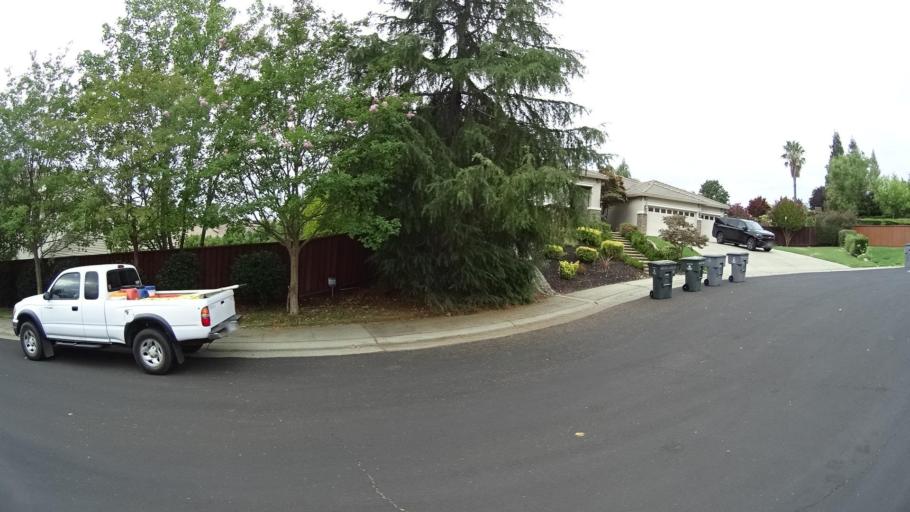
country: US
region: California
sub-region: Placer County
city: Rocklin
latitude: 38.7723
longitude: -121.2261
